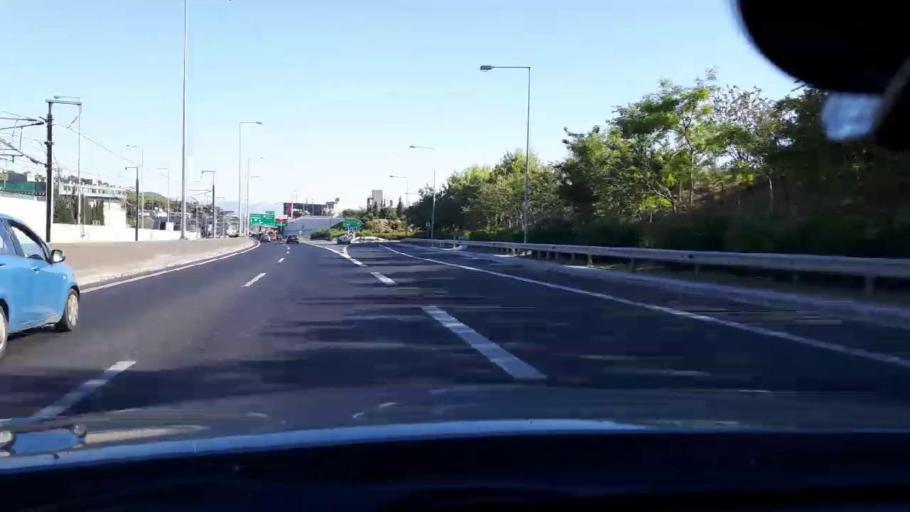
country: GR
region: Attica
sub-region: Nomarchia Anatolikis Attikis
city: Pallini
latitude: 37.9976
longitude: 23.8718
